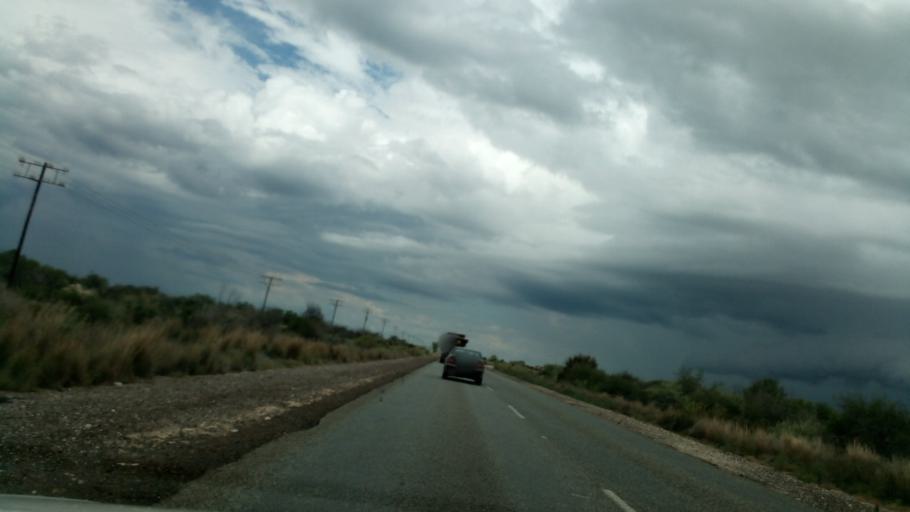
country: ZA
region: Northern Cape
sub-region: Frances Baard District Municipality
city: Barkly West
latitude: -28.2673
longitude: 24.0693
